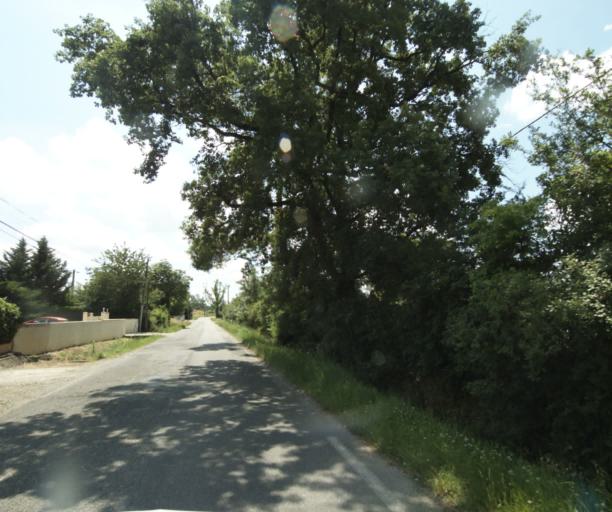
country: FR
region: Midi-Pyrenees
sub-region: Departement du Tarn-et-Garonne
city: Montauban
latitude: 44.0542
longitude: 1.3418
